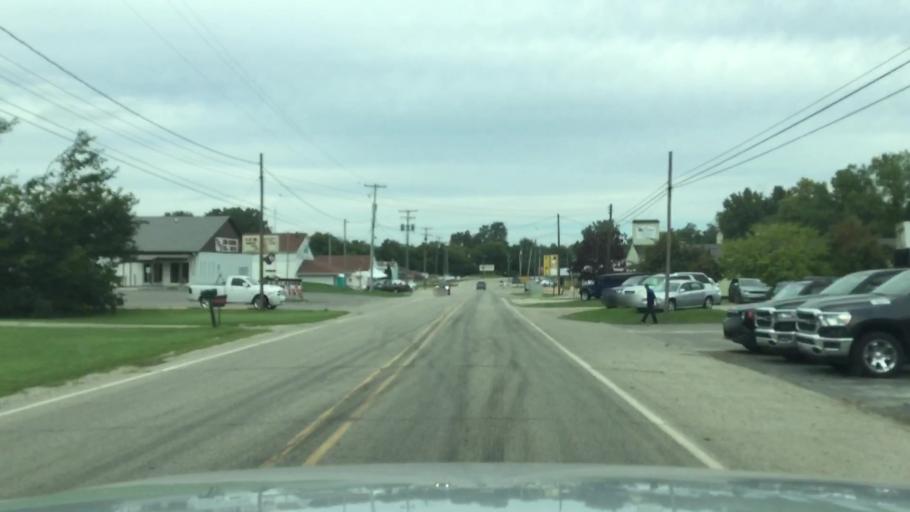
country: US
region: Michigan
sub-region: Shiawassee County
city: Durand
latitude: 42.9199
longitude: -83.9849
